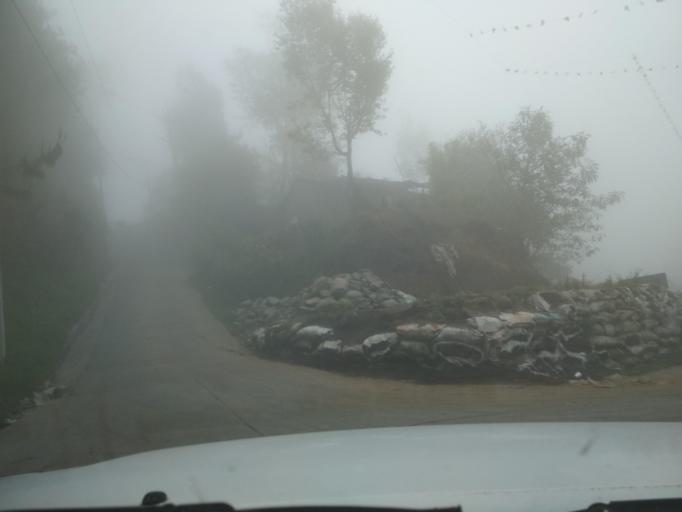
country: MX
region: Veracruz
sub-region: La Perla
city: Chilapa
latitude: 18.9781
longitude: -97.1911
